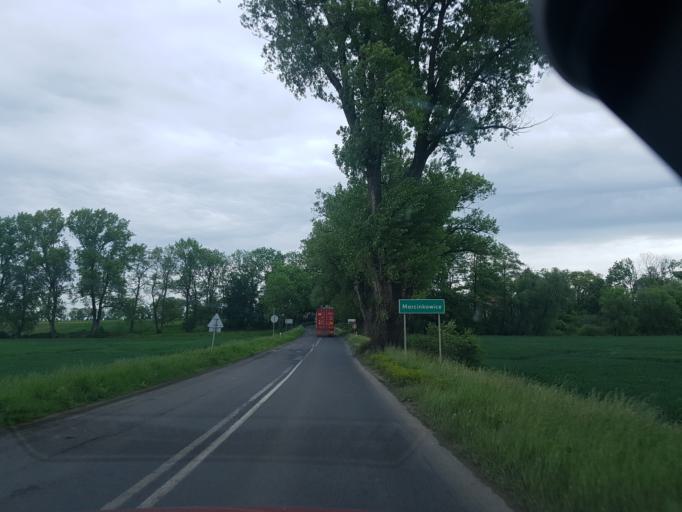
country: PL
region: Lower Silesian Voivodeship
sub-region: Powiat wroclawski
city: Zorawina
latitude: 50.9141
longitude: 16.9923
